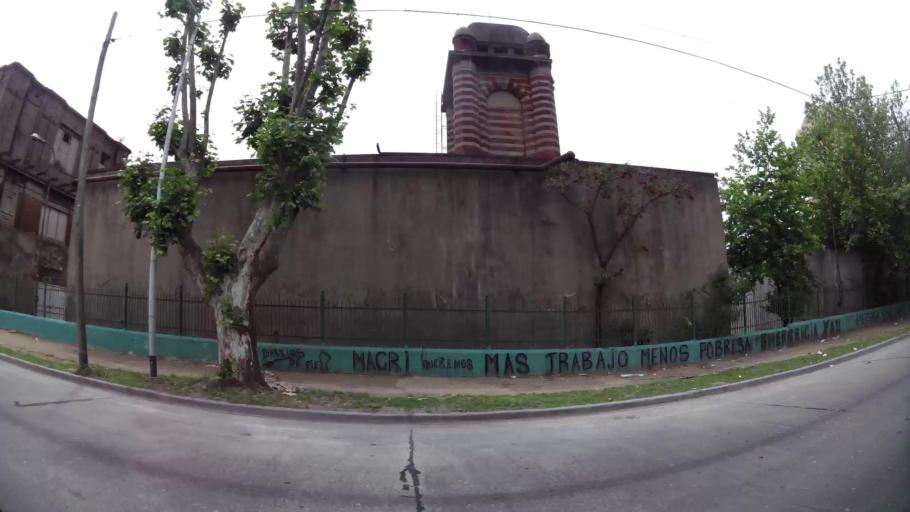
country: AR
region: Buenos Aires
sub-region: Partido de Avellaneda
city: Avellaneda
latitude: -34.6523
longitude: -58.3436
